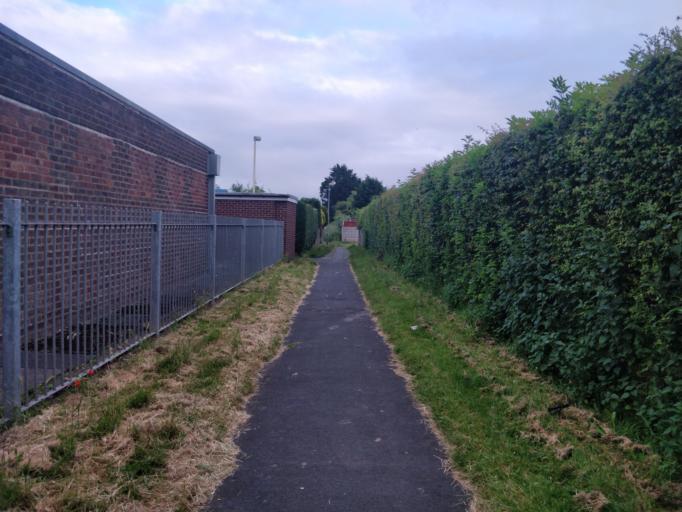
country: GB
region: England
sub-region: Lancashire
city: Banks
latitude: 53.6731
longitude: -2.9534
